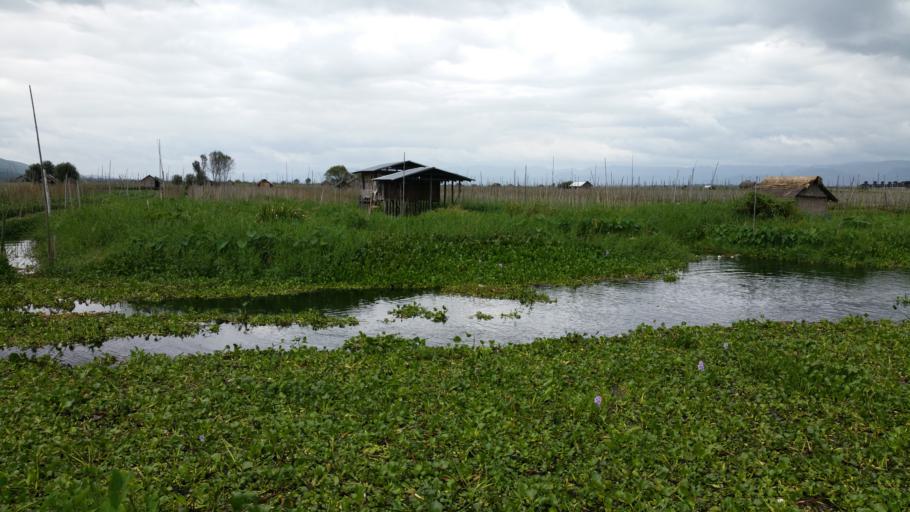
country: MM
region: Shan
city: Taunggyi
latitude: 20.5811
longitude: 96.9375
